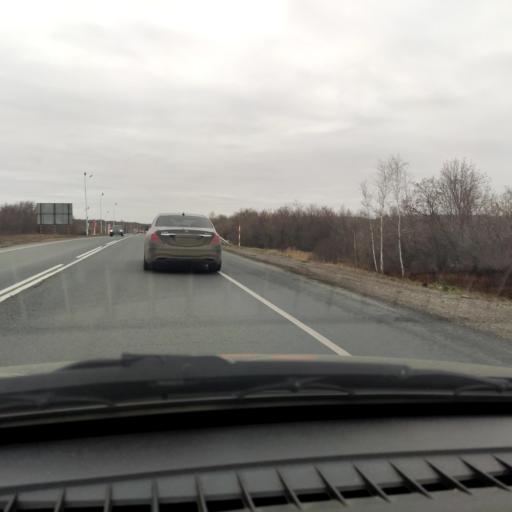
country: RU
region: Samara
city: Zhigulevsk
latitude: 53.3490
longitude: 49.4517
